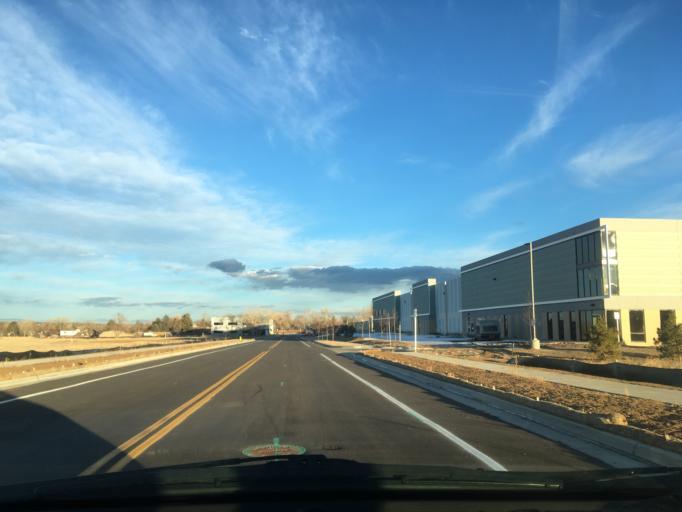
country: US
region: Colorado
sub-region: Jefferson County
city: Applewood
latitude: 39.8190
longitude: -105.1614
